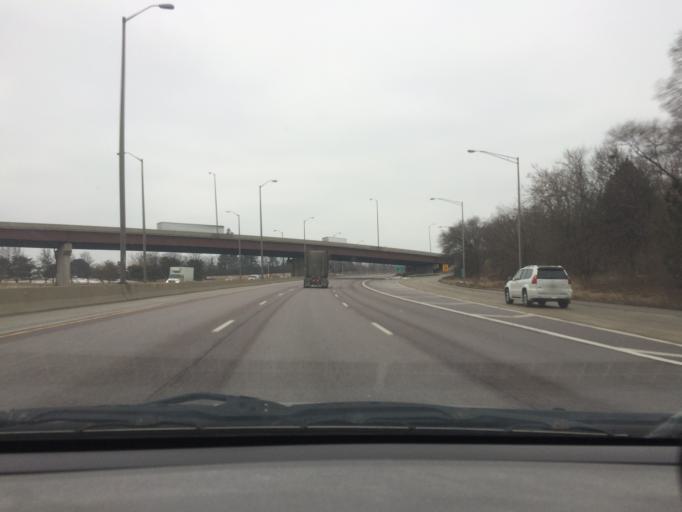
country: US
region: Illinois
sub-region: DuPage County
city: Itasca
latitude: 41.9597
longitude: -88.0267
